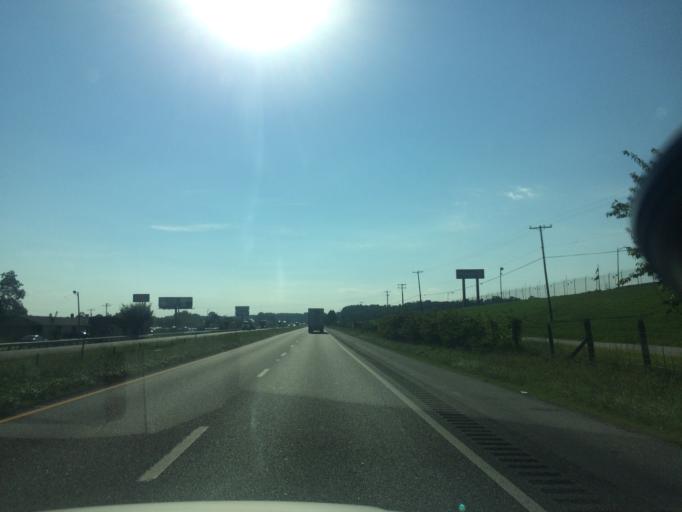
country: US
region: South Carolina
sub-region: Cherokee County
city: East Gaffney
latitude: 35.1028
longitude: -81.6283
